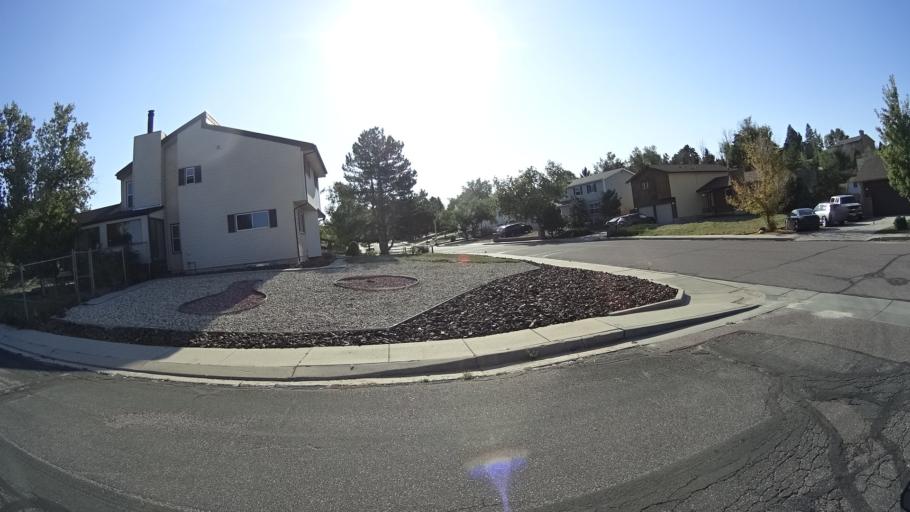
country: US
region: Colorado
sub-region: El Paso County
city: Cimarron Hills
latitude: 38.8919
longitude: -104.7303
